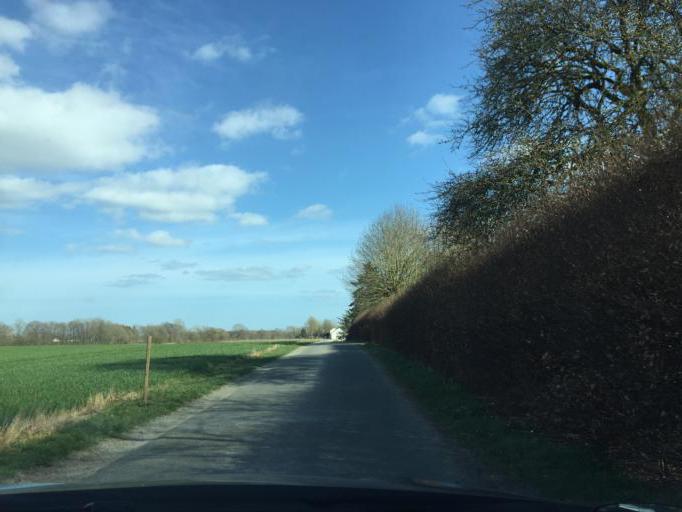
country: DK
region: South Denmark
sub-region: Kerteminde Kommune
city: Langeskov
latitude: 55.3065
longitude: 10.5560
